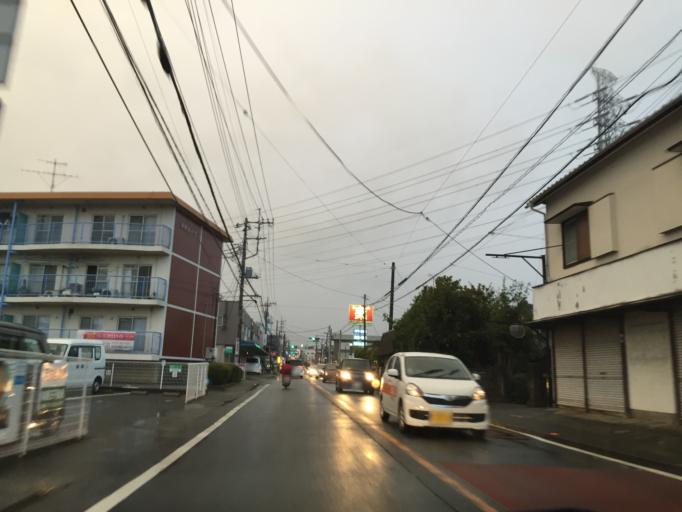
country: JP
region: Shizuoka
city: Mishima
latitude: 35.1409
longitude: 138.9123
